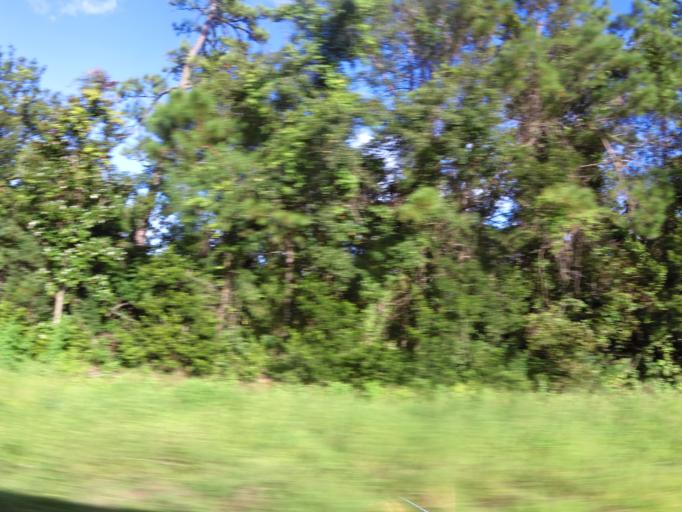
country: US
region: Georgia
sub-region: Glynn County
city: Country Club Estates
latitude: 31.2137
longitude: -81.4658
